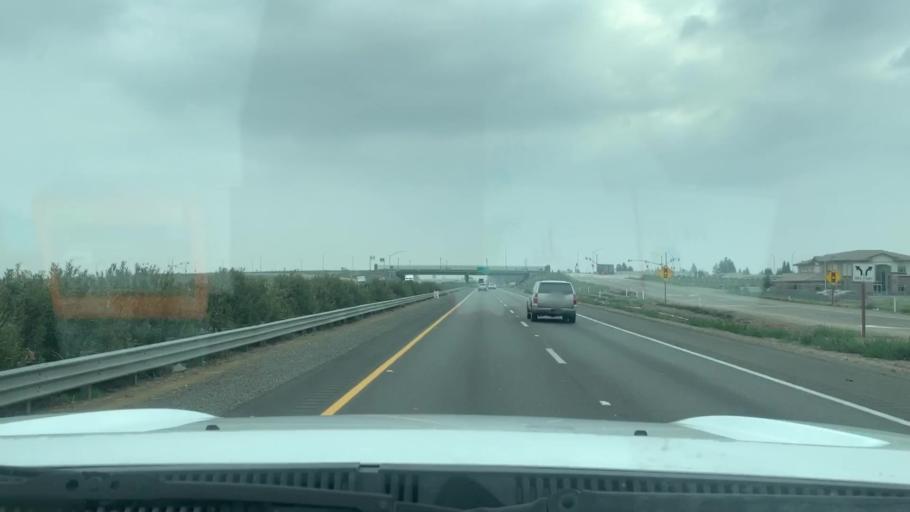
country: US
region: California
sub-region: Tulare County
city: Tulare
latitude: 36.2431
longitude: -119.3479
